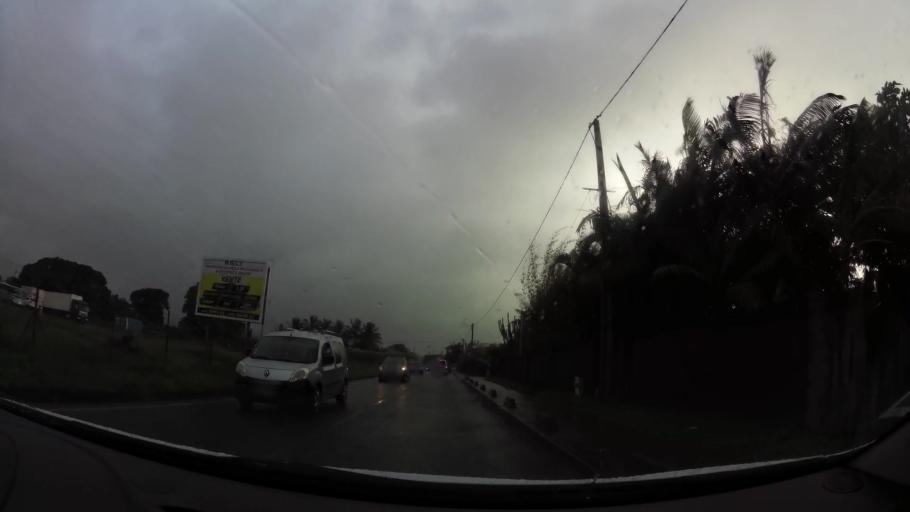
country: RE
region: Reunion
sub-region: Reunion
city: Saint-Andre
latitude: -20.9575
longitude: 55.6657
